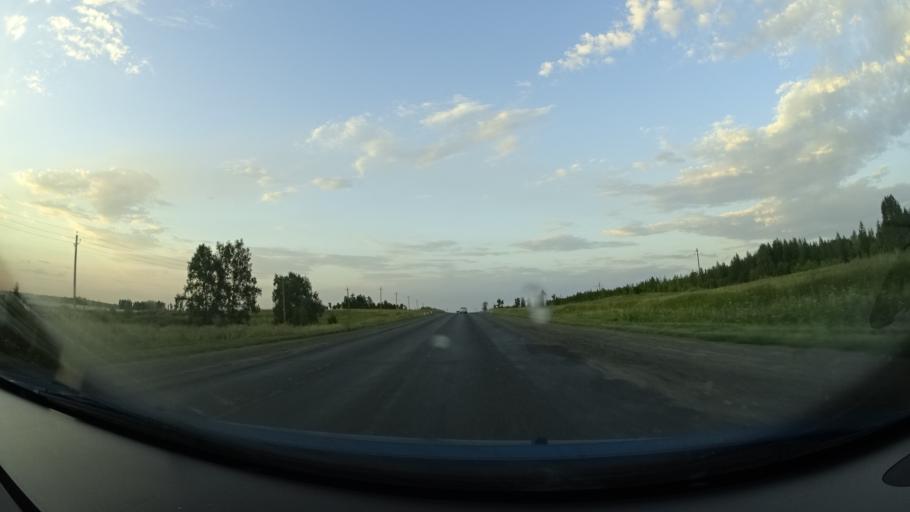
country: RU
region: Orenburg
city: Severnoye
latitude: 54.1865
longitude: 52.6674
